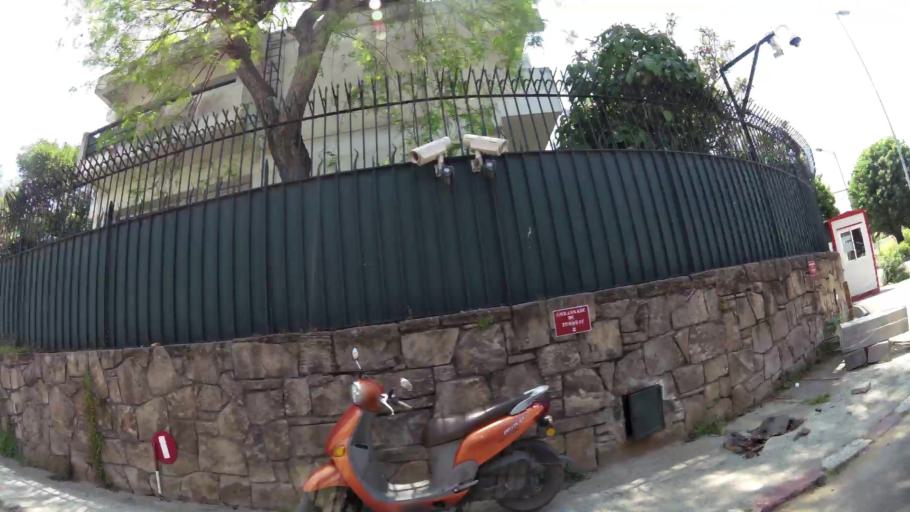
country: MA
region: Rabat-Sale-Zemmour-Zaer
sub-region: Rabat
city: Rabat
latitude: 34.0161
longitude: -6.8238
